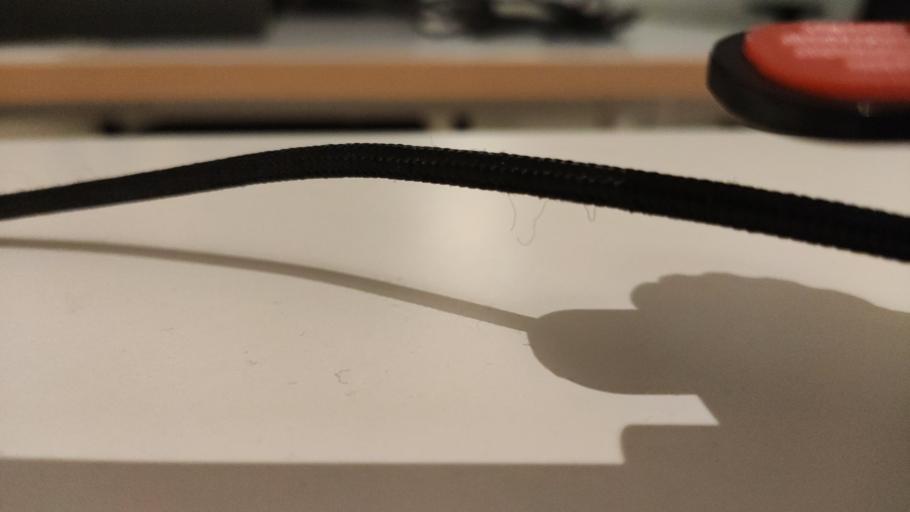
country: RU
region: Moskovskaya
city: Orekhovo-Zuyevo
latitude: 55.8421
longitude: 38.9667
